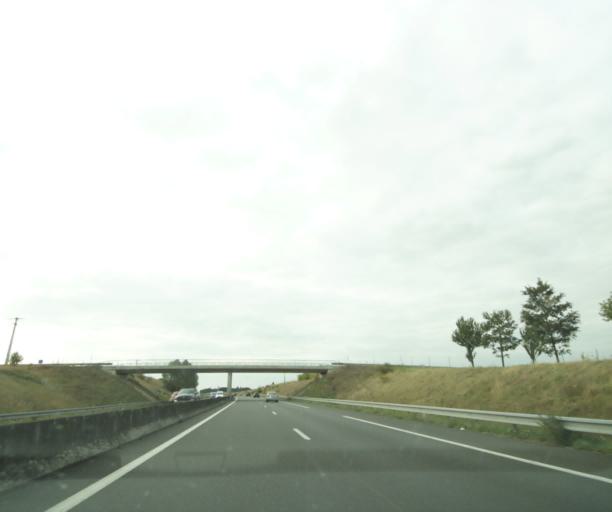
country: FR
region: Centre
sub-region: Departement d'Indre-et-Loire
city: Neuvy-le-Roi
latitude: 47.5820
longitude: 0.5700
